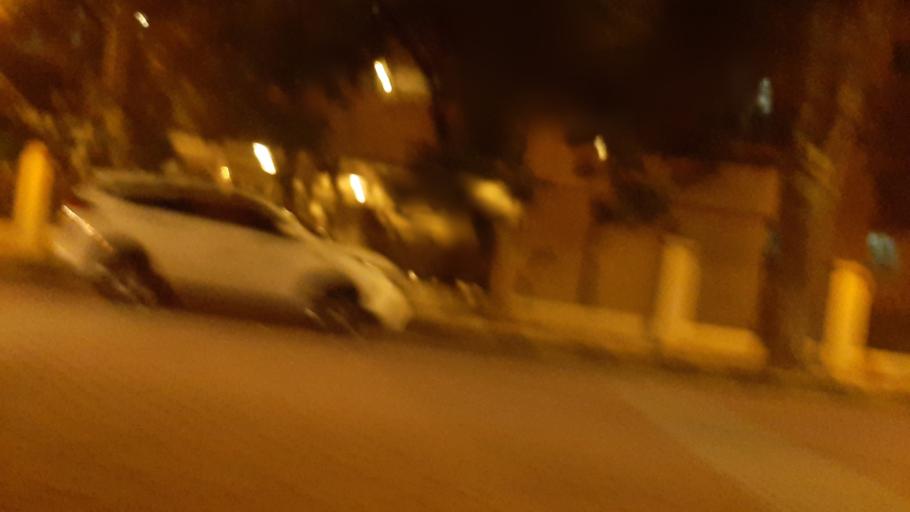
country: MY
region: Kuala Lumpur
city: Kuala Lumpur
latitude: 3.1699
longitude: 101.6535
